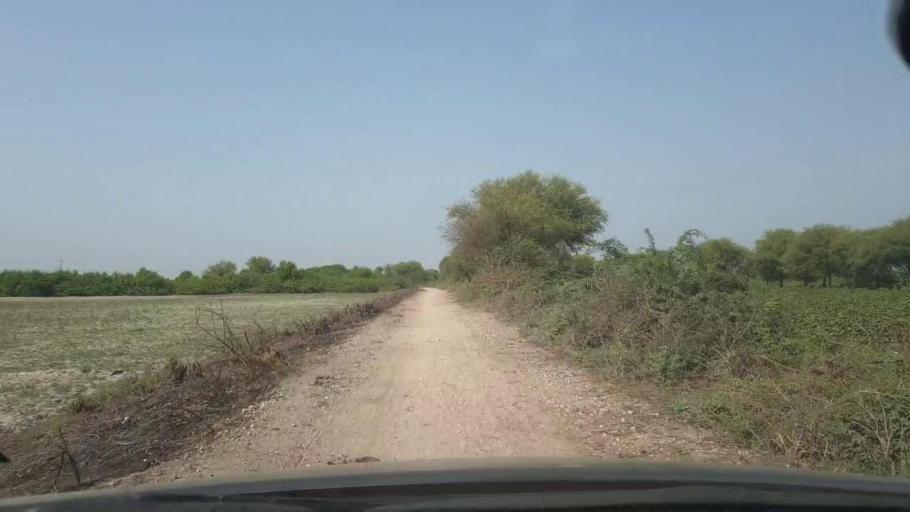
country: PK
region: Sindh
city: Naukot
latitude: 24.7994
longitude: 69.2410
